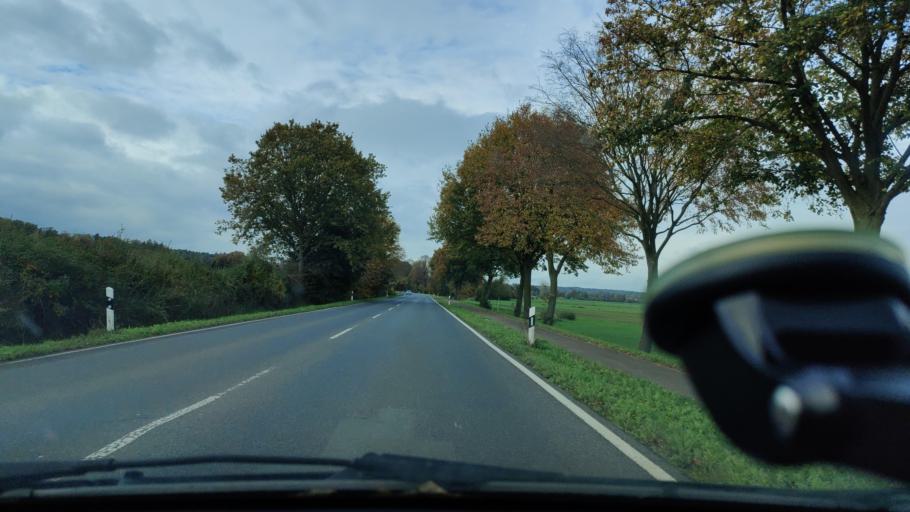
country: DE
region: North Rhine-Westphalia
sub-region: Regierungsbezirk Dusseldorf
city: Sonsbeck
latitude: 51.6348
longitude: 6.4039
